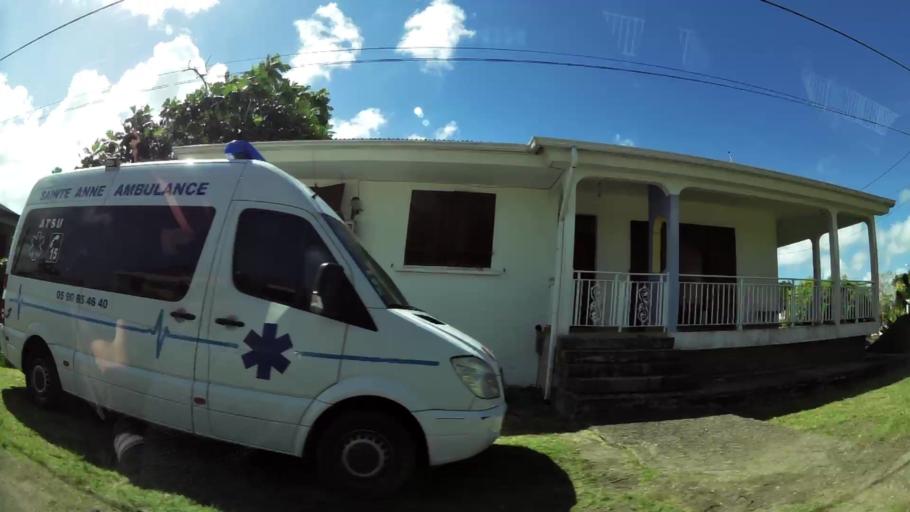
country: GP
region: Guadeloupe
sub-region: Guadeloupe
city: Petit-Canal
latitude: 16.3555
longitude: -61.4246
